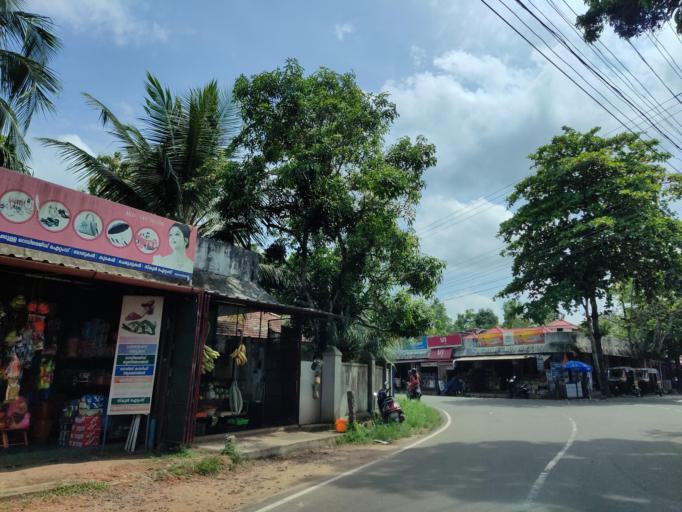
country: IN
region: Kerala
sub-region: Alappuzha
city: Mavelikara
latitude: 9.2762
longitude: 76.5670
